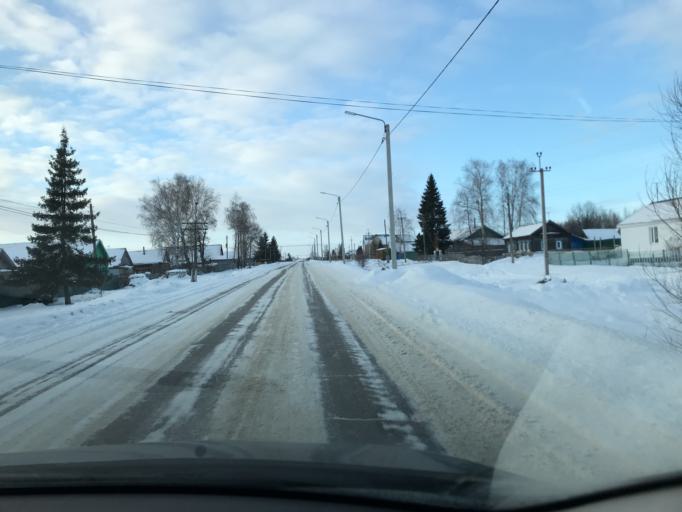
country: RU
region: Ulyanovsk
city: Undory
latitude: 54.6035
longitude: 48.4128
